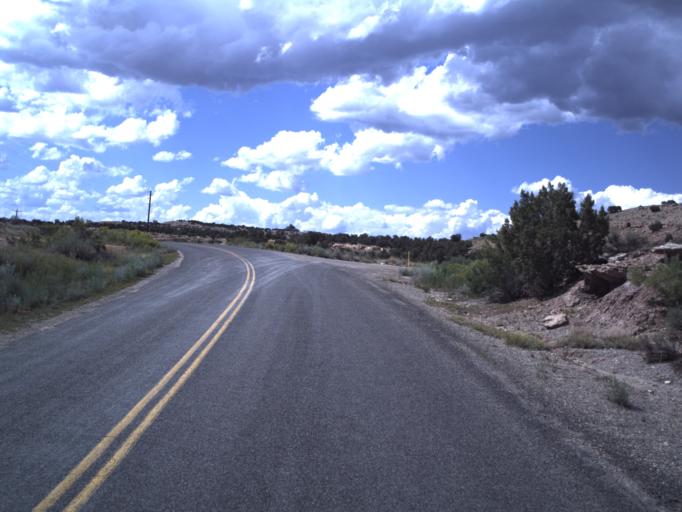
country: US
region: Utah
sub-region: Duchesne County
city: Duchesne
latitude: 40.1760
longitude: -110.4436
